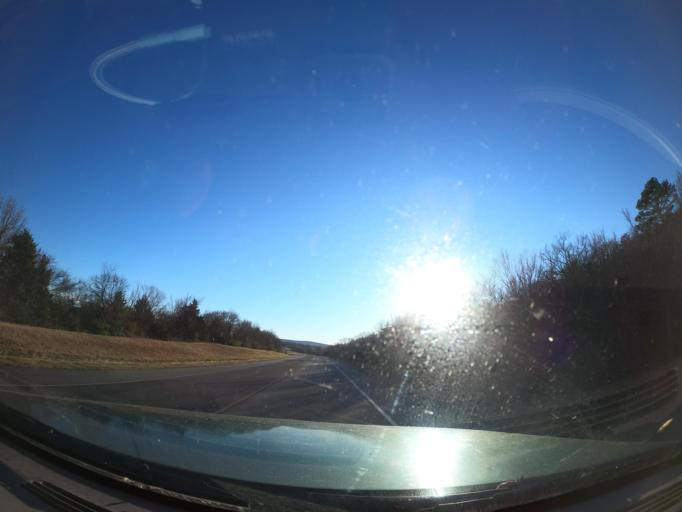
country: US
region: Oklahoma
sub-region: Pittsburg County
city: Hartshorne
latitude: 34.8573
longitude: -95.5324
